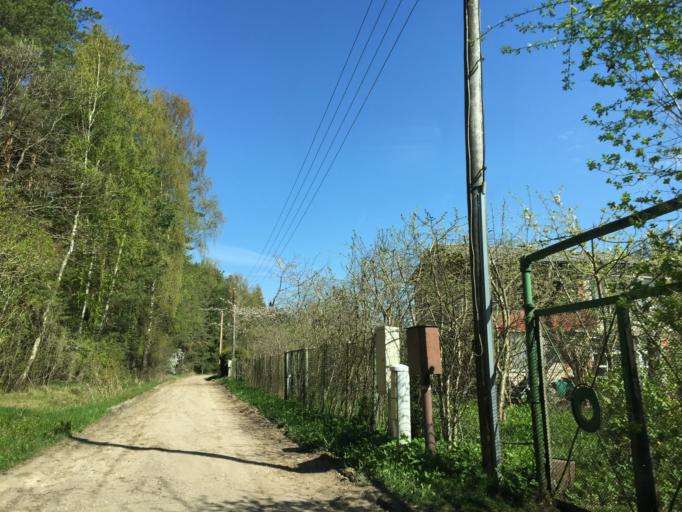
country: LV
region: Saulkrastu
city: Saulkrasti
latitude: 57.3144
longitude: 24.4349
